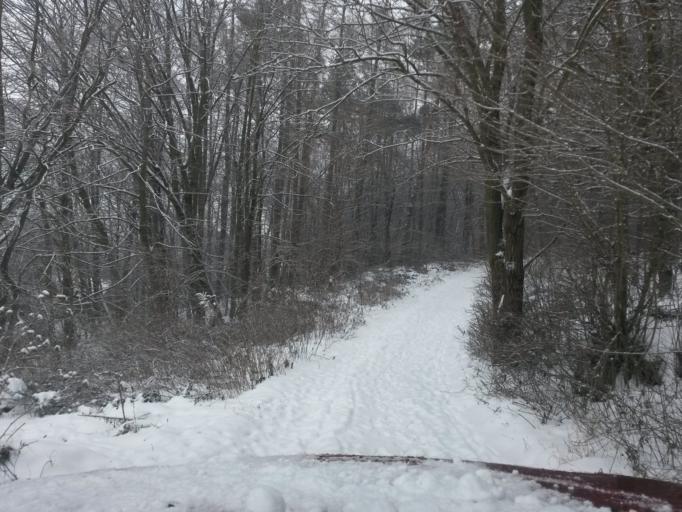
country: SK
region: Kosicky
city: Kosice
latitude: 48.7231
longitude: 21.3048
